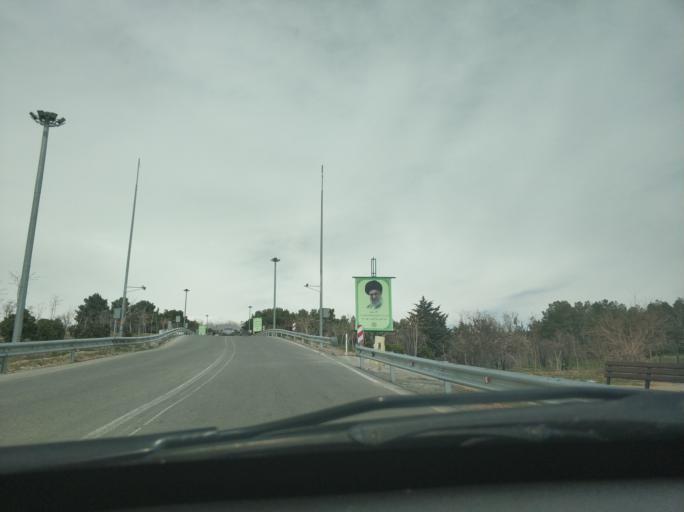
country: IR
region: Tehran
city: Tajrish
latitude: 35.7735
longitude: 51.5514
